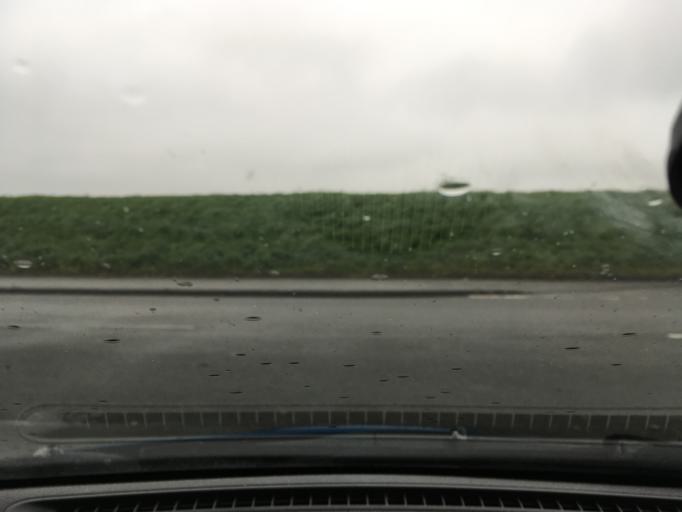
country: DE
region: Hamburg
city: Rothenburgsort
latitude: 53.4962
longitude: 10.0432
